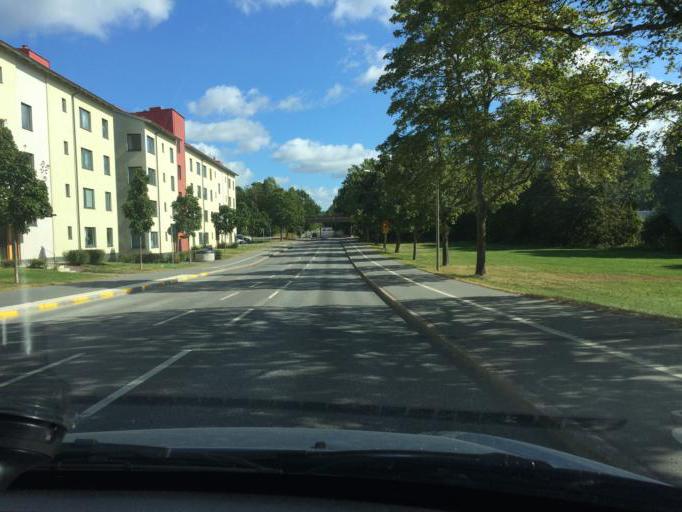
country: SE
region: Stockholm
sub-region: Nacka Kommun
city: Nacka
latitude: 59.2797
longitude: 18.1164
